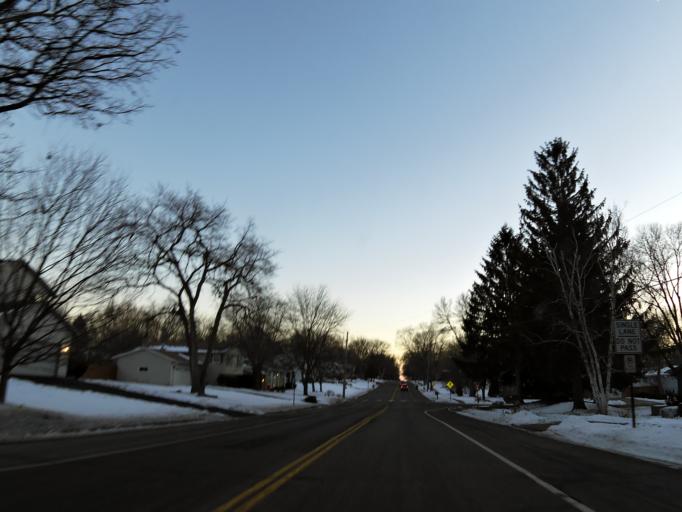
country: US
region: Minnesota
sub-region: Scott County
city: Savage
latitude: 44.8150
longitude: -93.3584
